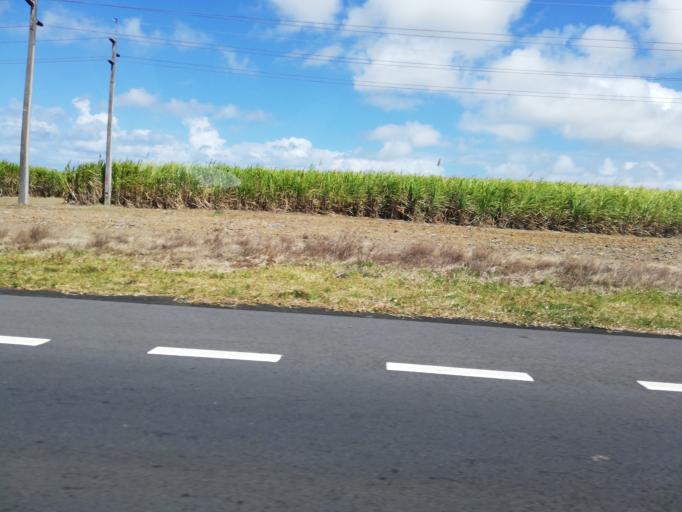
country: MU
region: Grand Port
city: Plaine Magnien
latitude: -20.4370
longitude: 57.6517
